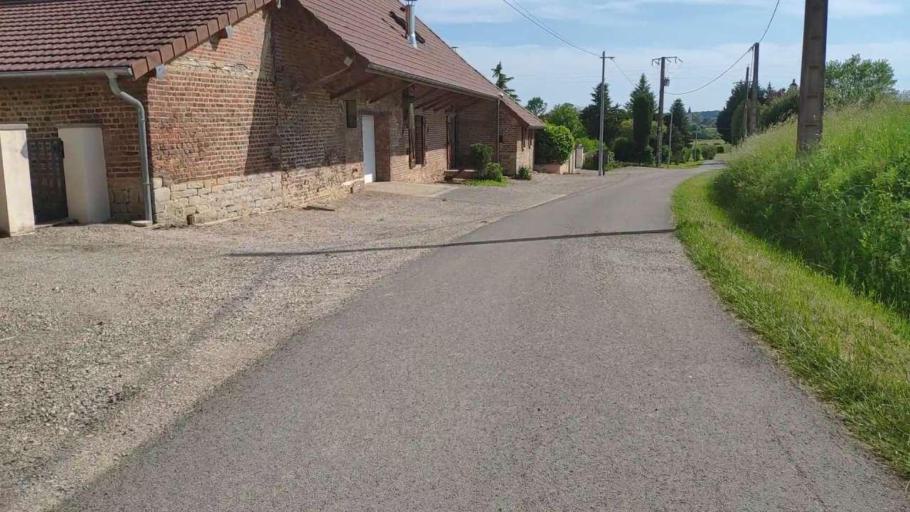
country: FR
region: Franche-Comte
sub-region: Departement du Jura
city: Bletterans
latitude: 46.8103
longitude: 5.3849
